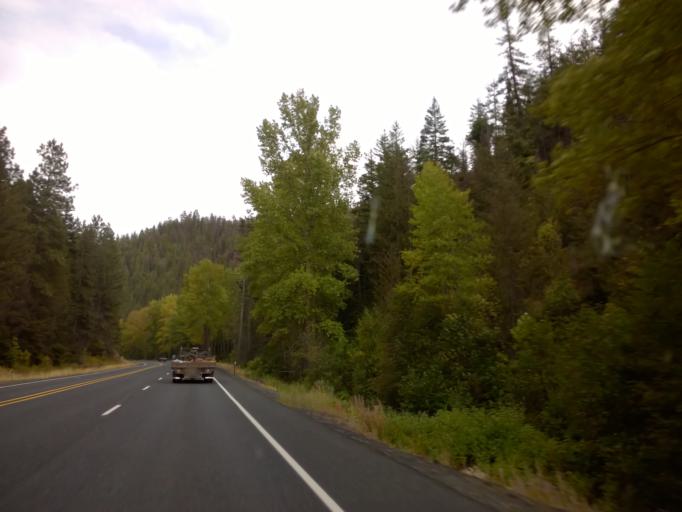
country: US
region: Washington
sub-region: Chelan County
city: Leavenworth
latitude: 47.3943
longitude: -120.6462
